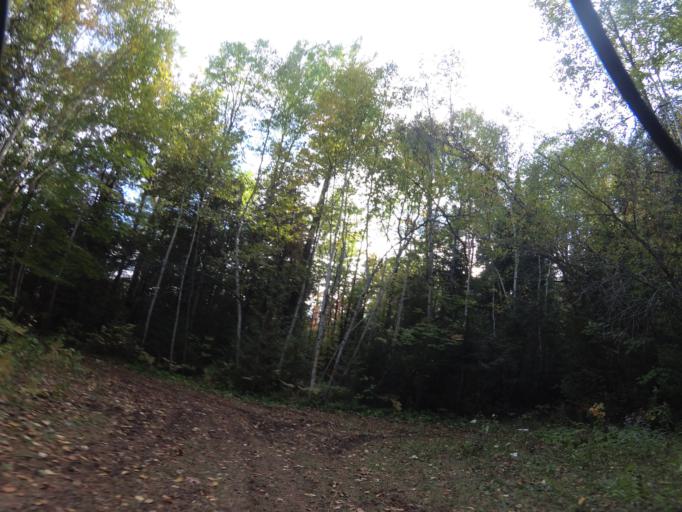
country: CA
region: Ontario
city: Pembroke
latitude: 45.3436
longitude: -77.1759
